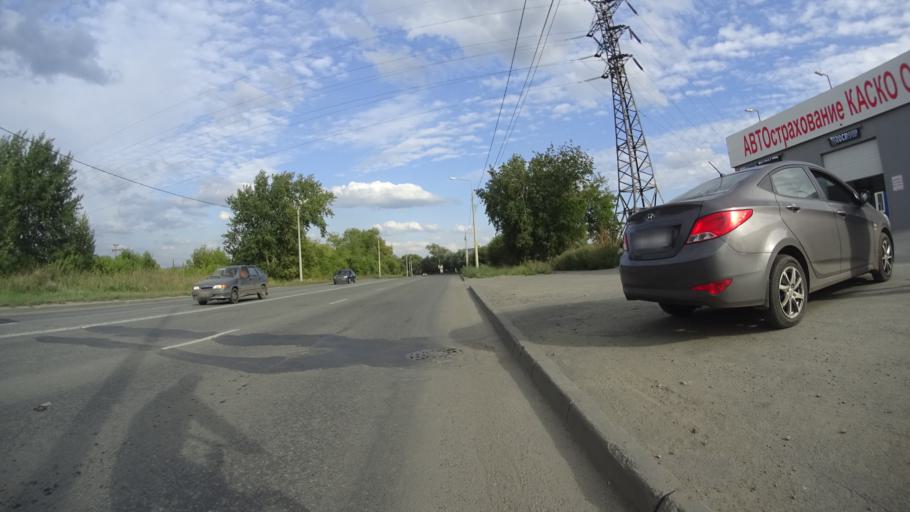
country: RU
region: Chelyabinsk
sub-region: Gorod Chelyabinsk
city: Chelyabinsk
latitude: 55.1966
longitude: 61.3739
